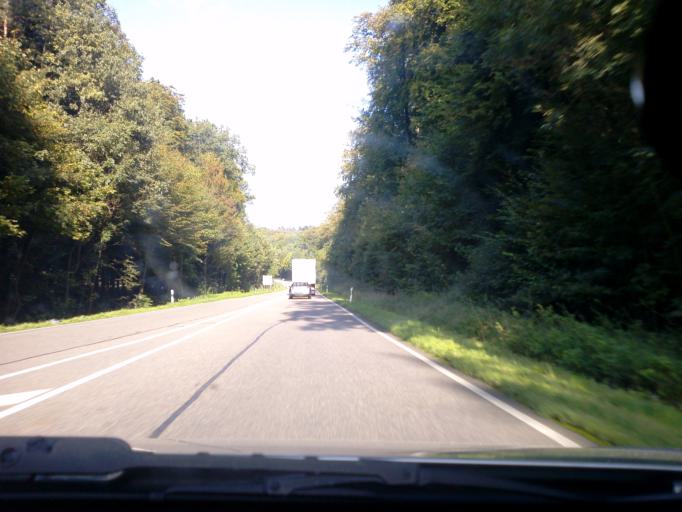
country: DE
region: Baden-Wuerttemberg
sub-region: Karlsruhe Region
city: Knittlingen
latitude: 49.0648
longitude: 8.7541
